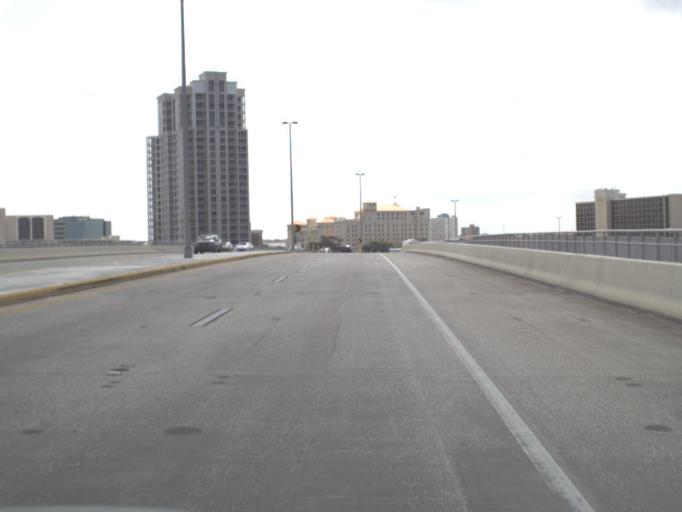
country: US
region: Florida
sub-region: Pinellas County
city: Clearwater
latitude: 27.9664
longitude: -82.8064
